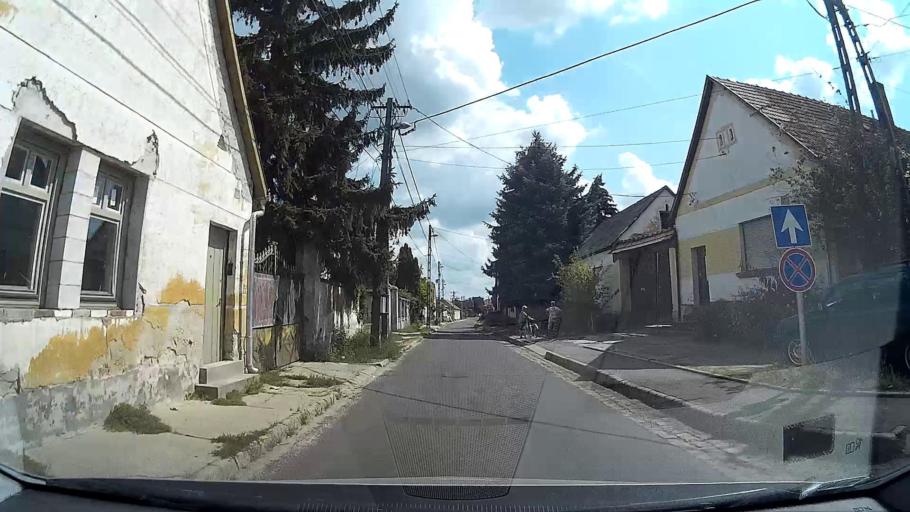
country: HU
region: Pest
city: Tahitotfalu
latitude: 47.7525
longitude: 19.0922
